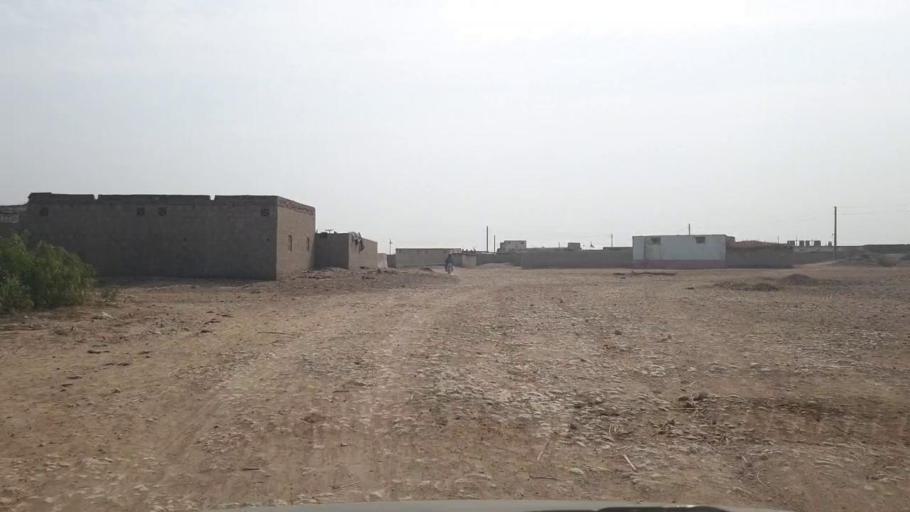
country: PK
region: Sindh
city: Tando Muhammad Khan
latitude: 25.1583
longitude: 68.4709
